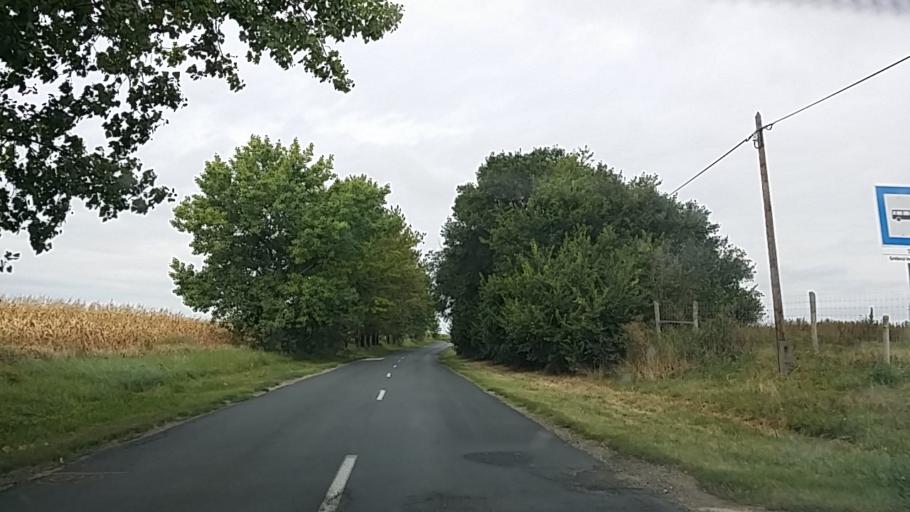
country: HU
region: Komarom-Esztergom
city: Tata
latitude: 47.6564
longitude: 18.2806
